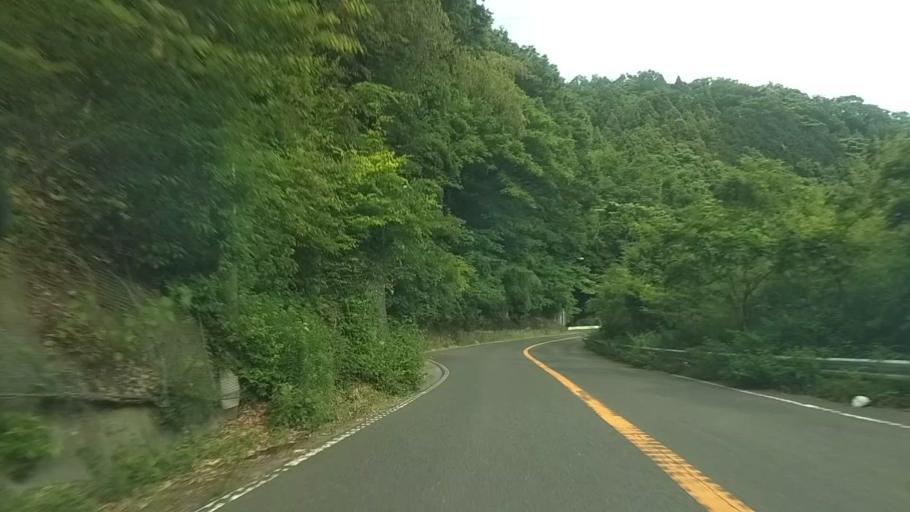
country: JP
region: Shizuoka
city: Gotemba
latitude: 35.3643
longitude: 139.0550
